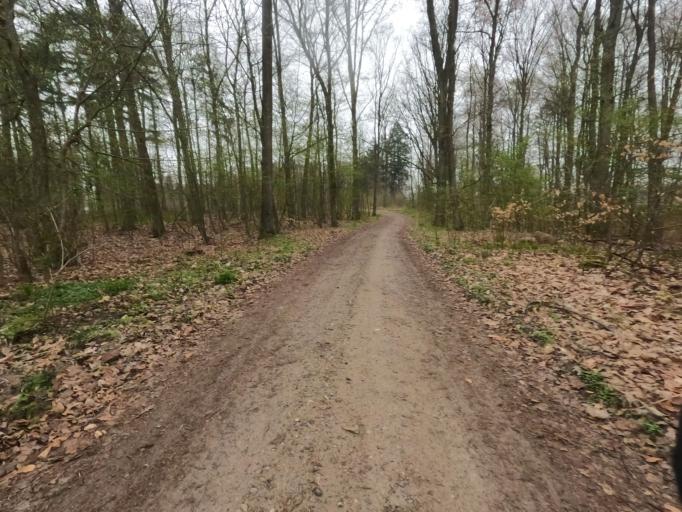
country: PL
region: West Pomeranian Voivodeship
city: Trzcinsko Zdroj
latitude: 52.9311
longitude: 14.6862
